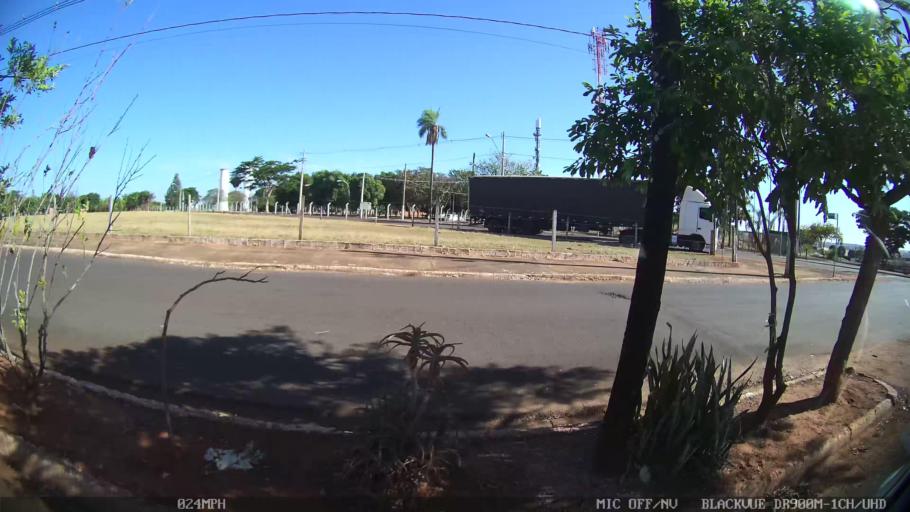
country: BR
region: Sao Paulo
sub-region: Olimpia
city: Olimpia
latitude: -20.7439
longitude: -48.8929
